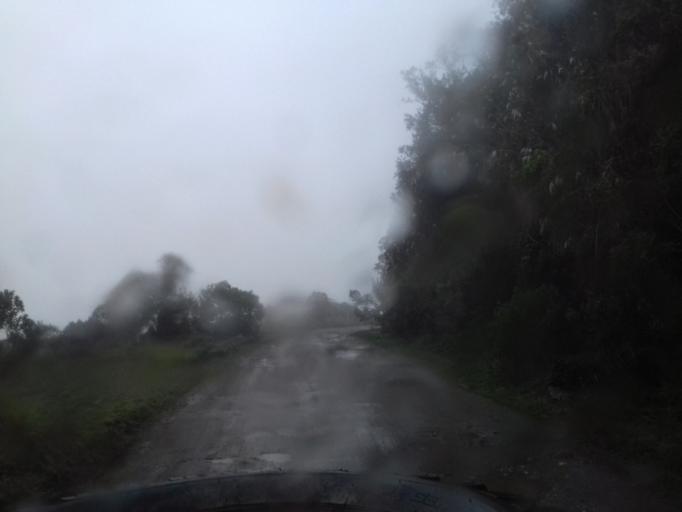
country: CO
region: Tolima
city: Murillo
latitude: 4.8901
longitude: -75.2580
